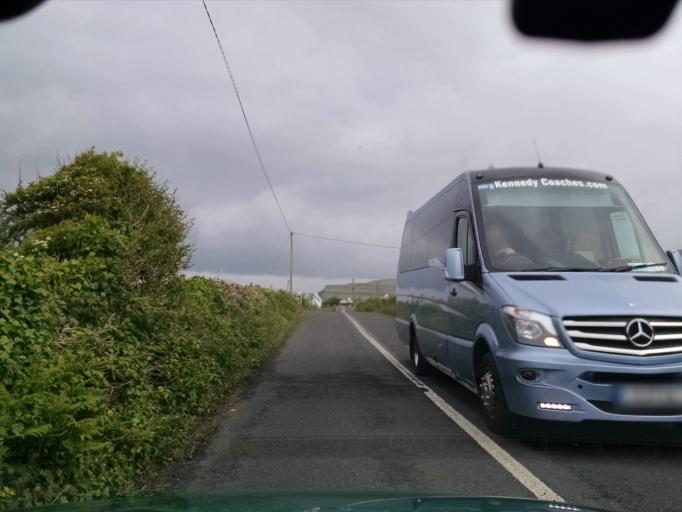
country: IE
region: Connaught
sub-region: County Galway
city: Bearna
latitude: 53.1230
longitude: -9.2781
